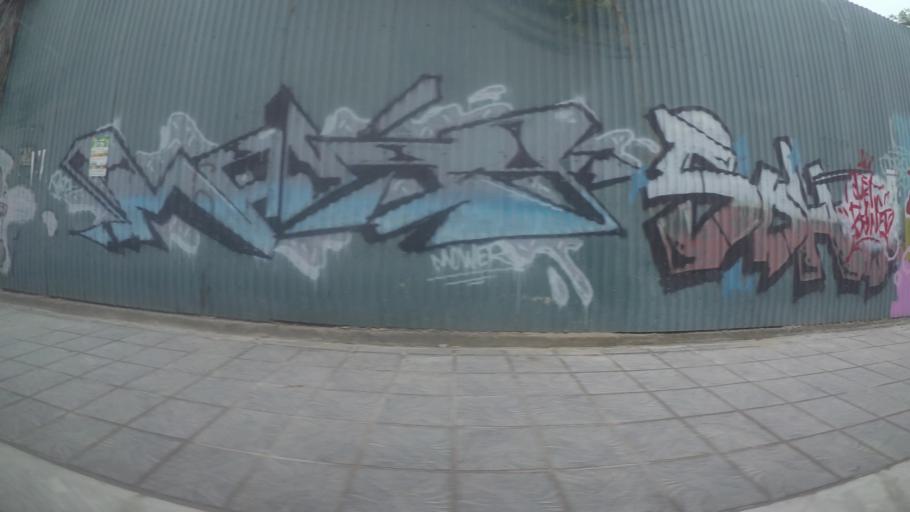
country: VN
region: Ha Noi
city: Tay Ho
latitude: 21.0628
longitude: 105.8204
